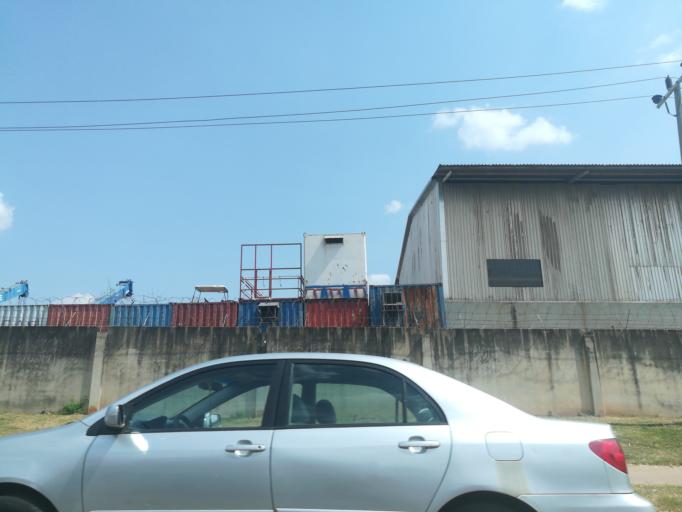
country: NG
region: Abuja Federal Capital Territory
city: Abuja
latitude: 9.0635
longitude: 7.4462
